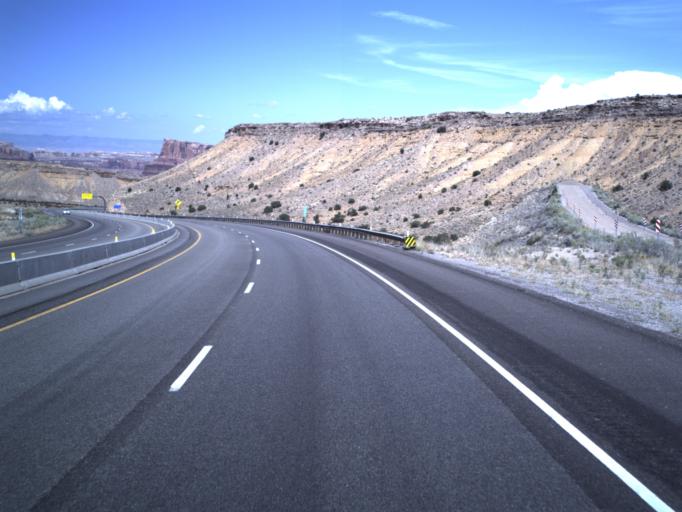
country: US
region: Utah
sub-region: Emery County
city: Castle Dale
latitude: 38.9314
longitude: -110.4896
